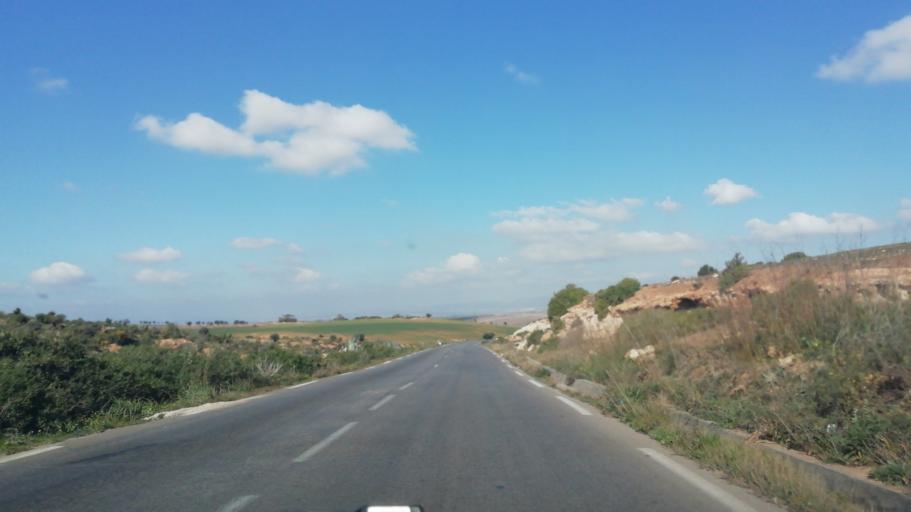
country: DZ
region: Oran
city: Ain el Bya
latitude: 35.7220
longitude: -0.2421
